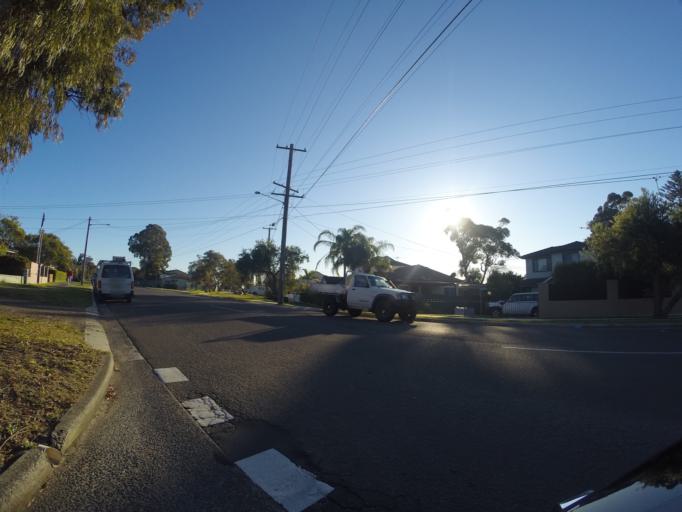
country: AU
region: New South Wales
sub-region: Sutherland Shire
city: Gymea Bay
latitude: -34.0517
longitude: 151.0881
